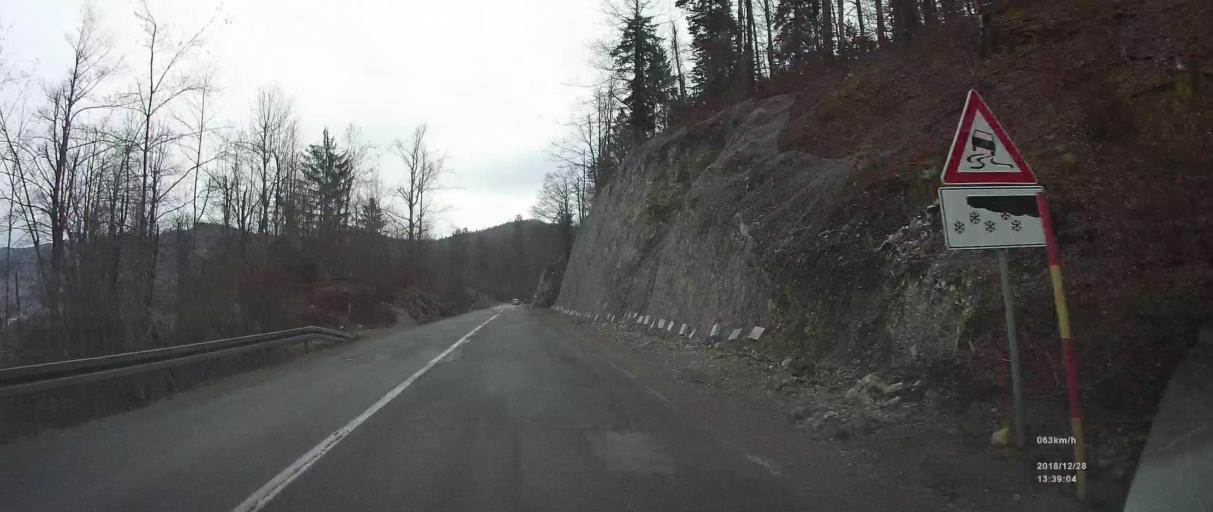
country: HR
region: Primorsko-Goranska
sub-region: Grad Delnice
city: Delnice
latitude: 45.3527
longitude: 14.7321
